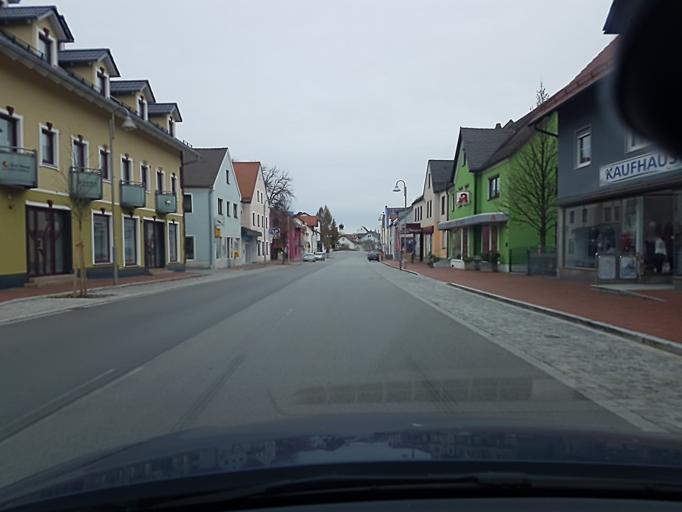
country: DE
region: Bavaria
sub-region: Lower Bavaria
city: Ergoldsbach
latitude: 48.7335
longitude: 12.1896
